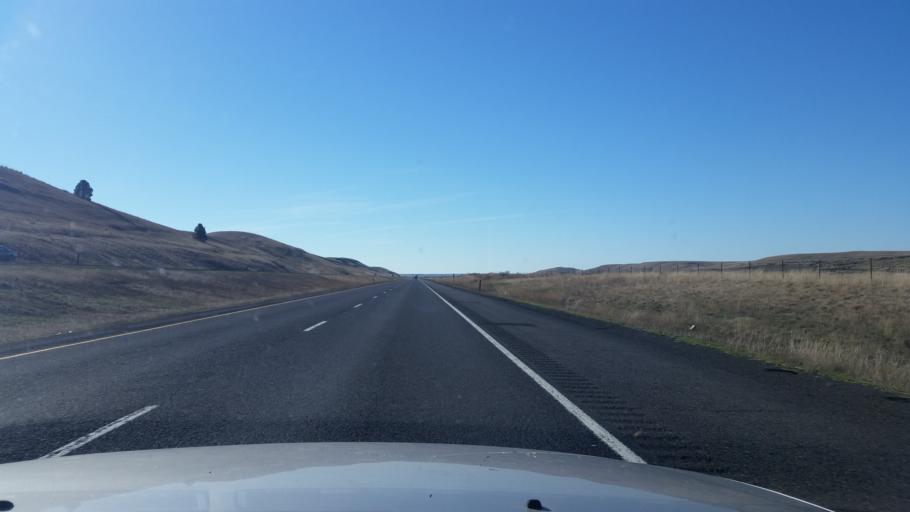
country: US
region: Washington
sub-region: Spokane County
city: Medical Lake
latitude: 47.3661
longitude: -117.8840
